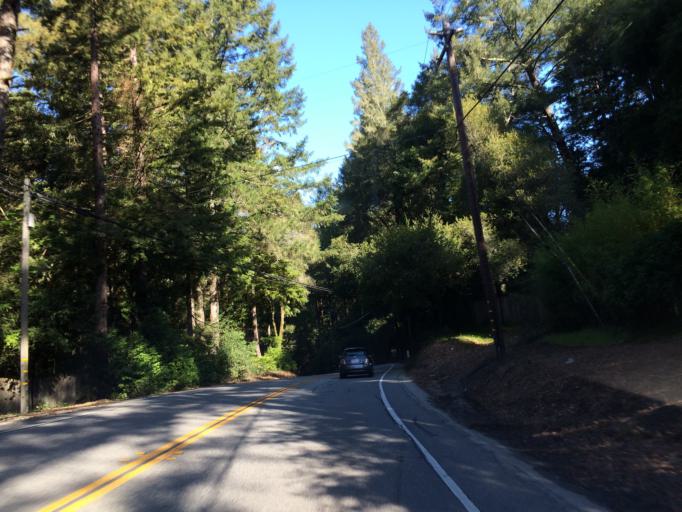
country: US
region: California
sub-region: Santa Cruz County
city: Boulder Creek
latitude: 37.1356
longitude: -122.1276
